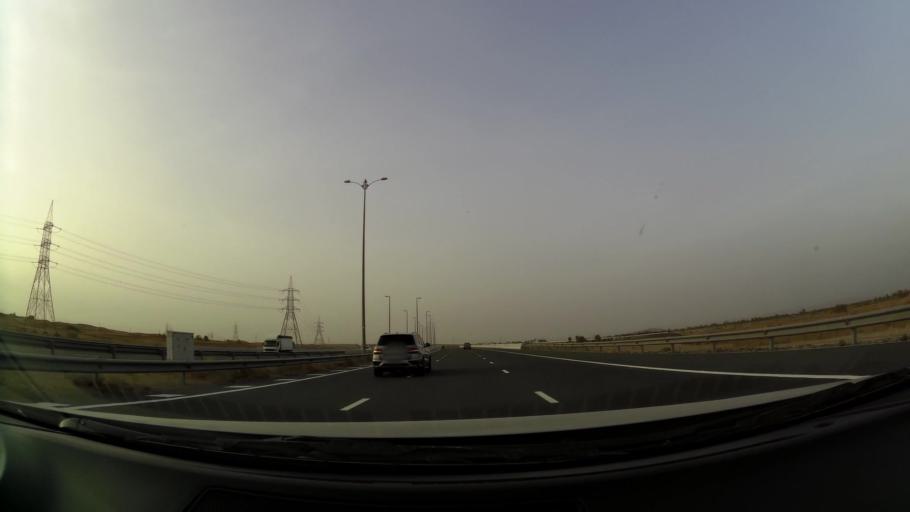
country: OM
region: Al Buraimi
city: Al Buraymi
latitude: 24.3714
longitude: 55.7954
